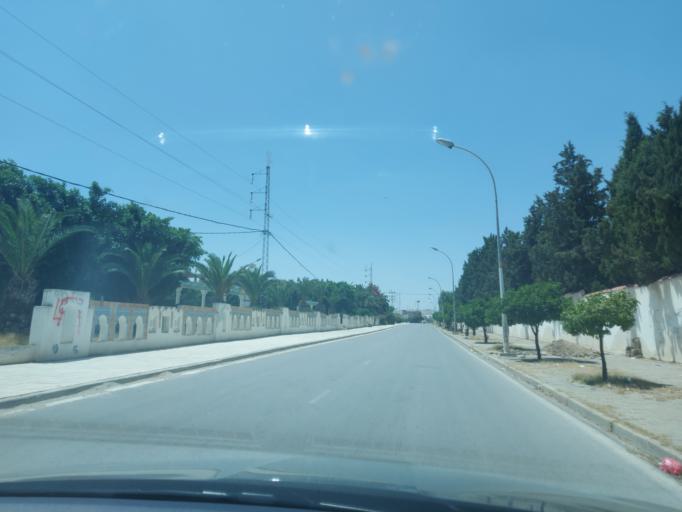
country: TN
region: Silyanah
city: Siliana
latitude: 36.0852
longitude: 9.3609
